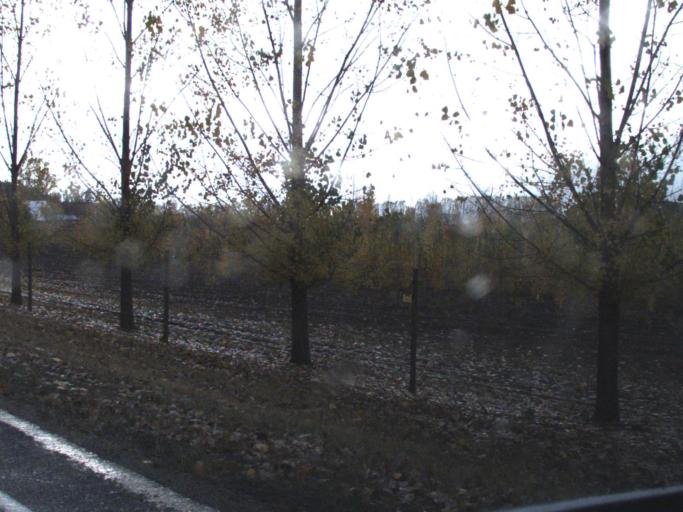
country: US
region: Washington
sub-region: Stevens County
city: Kettle Falls
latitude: 48.4732
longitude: -118.1698
